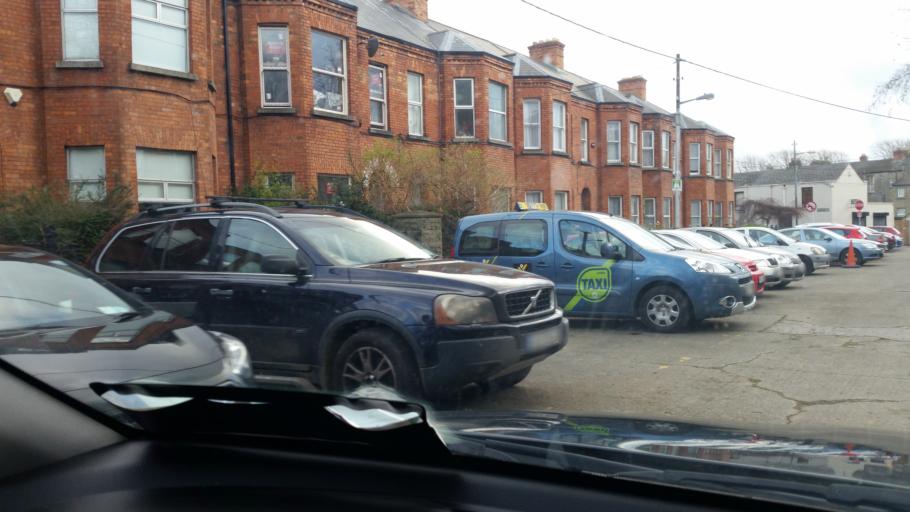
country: IE
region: Leinster
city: Cabra
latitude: 53.3556
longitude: -6.2953
